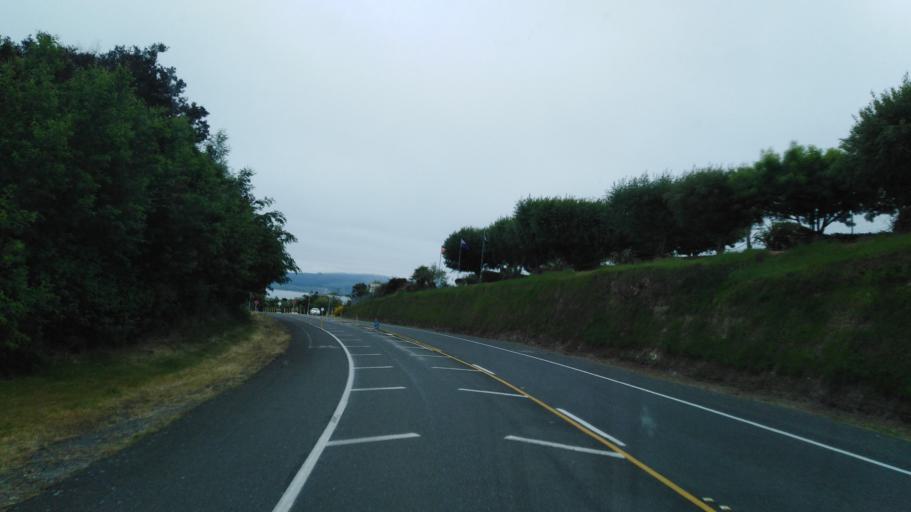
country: NZ
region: Waikato
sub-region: Taupo District
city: Taupo
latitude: -38.7039
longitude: 176.0985
